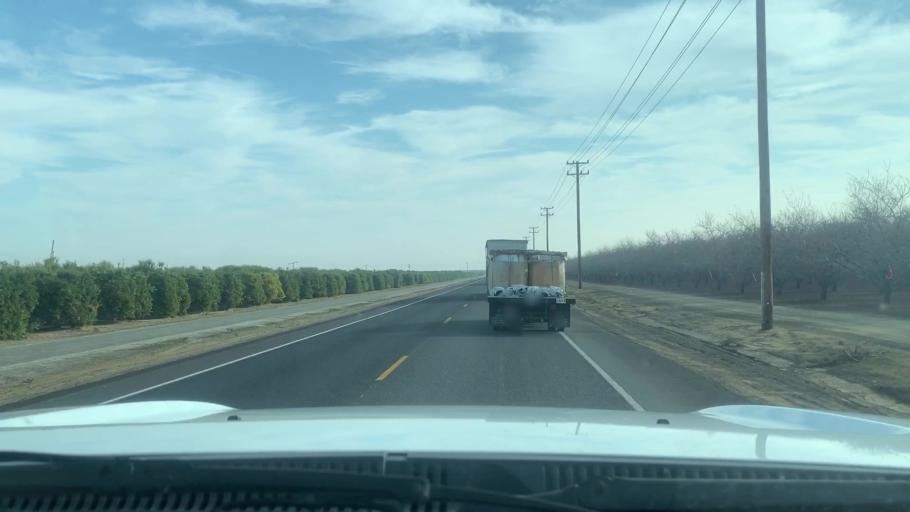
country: US
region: California
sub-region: Kern County
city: Lost Hills
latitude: 35.4991
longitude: -119.7323
